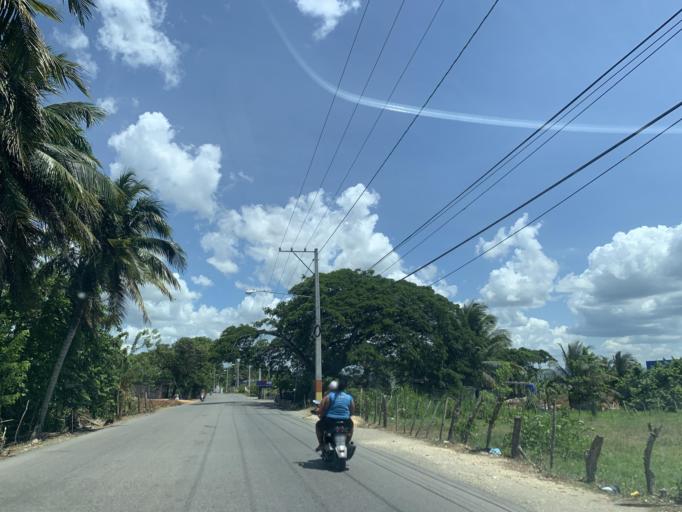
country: DO
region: Puerto Plata
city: Cabarete
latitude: 19.6939
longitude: -70.3810
